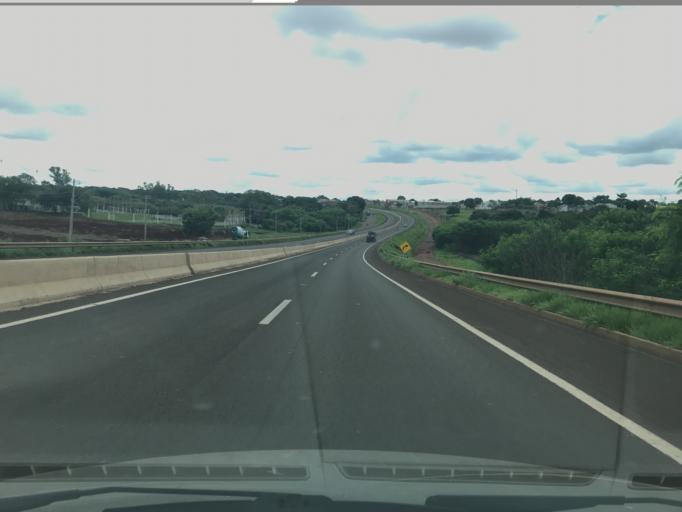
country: BR
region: Parana
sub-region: Maringa
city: Maringa
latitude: -23.3721
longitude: -51.9261
